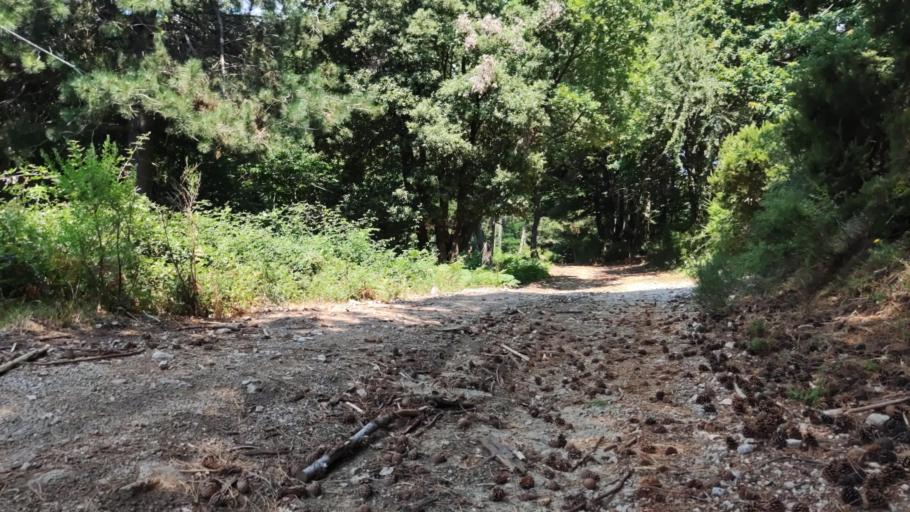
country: IT
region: Calabria
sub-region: Provincia di Reggio Calabria
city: Pazzano
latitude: 38.4660
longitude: 16.3987
